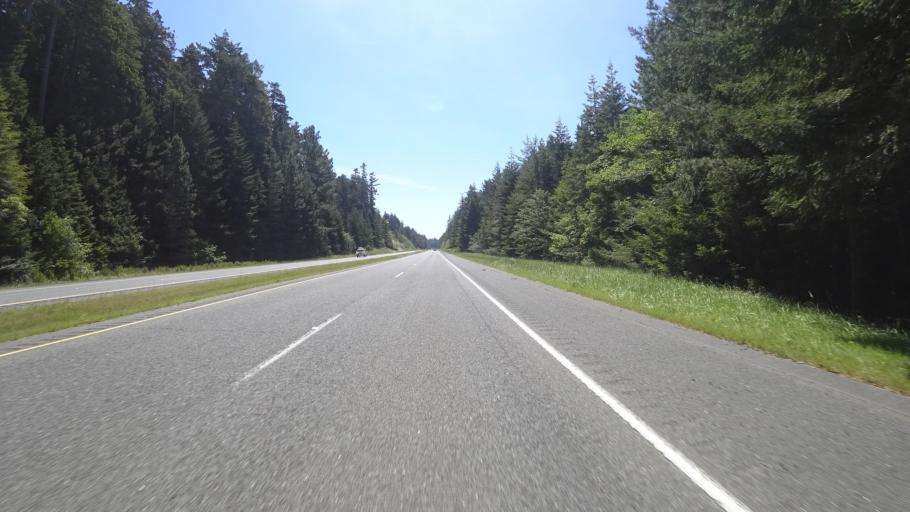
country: US
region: California
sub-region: Humboldt County
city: Westhaven-Moonstone
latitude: 41.0857
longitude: -124.1472
